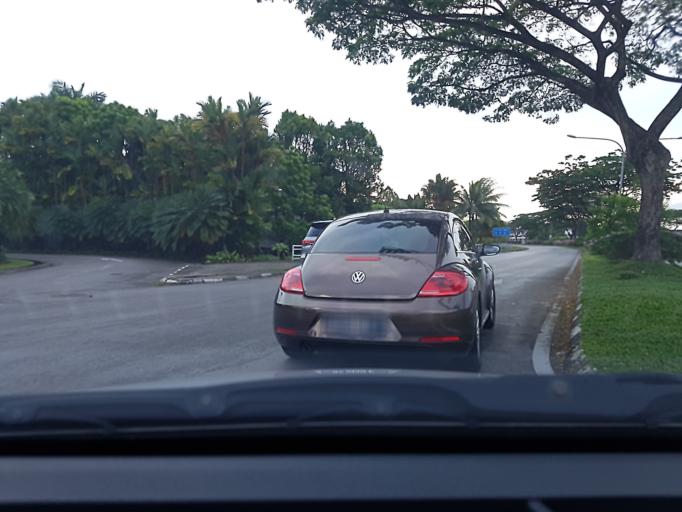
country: MY
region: Sarawak
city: Kuching
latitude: 1.5165
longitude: 110.3670
